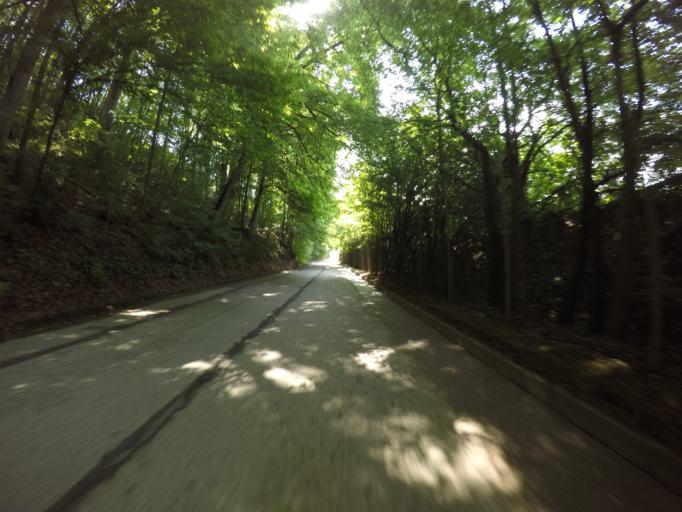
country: DE
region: Baden-Wuerttemberg
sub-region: Tuebingen Region
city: Tuebingen
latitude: 48.5126
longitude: 9.0859
